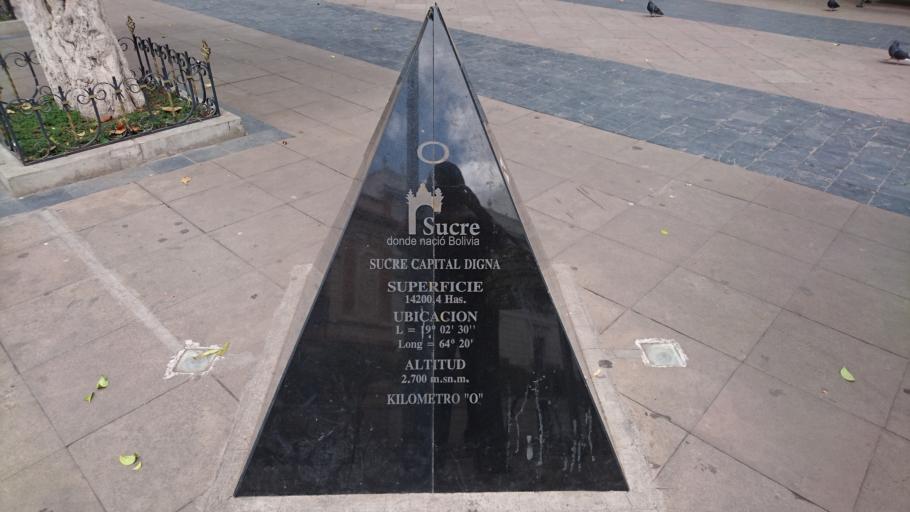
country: BO
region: Chuquisaca
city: Sucre
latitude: -19.0478
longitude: -65.2598
